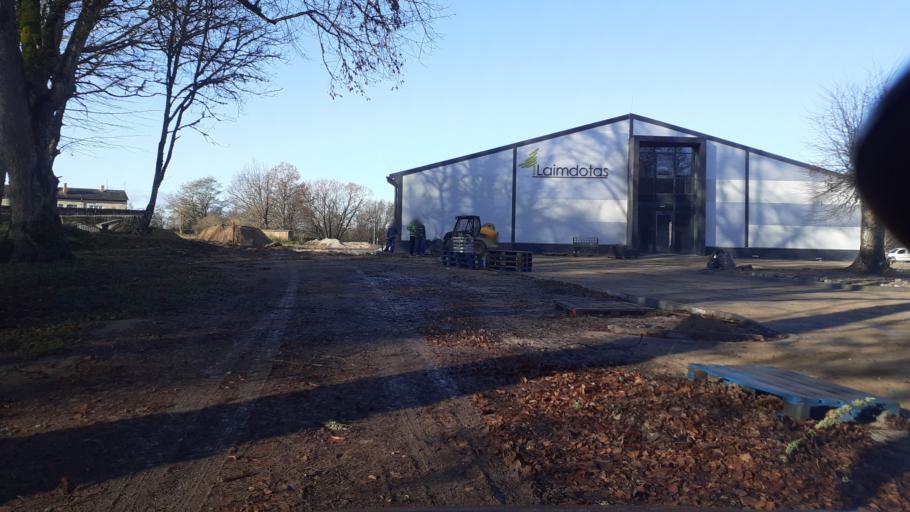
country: LV
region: Kuldigas Rajons
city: Kuldiga
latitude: 56.9997
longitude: 21.8873
